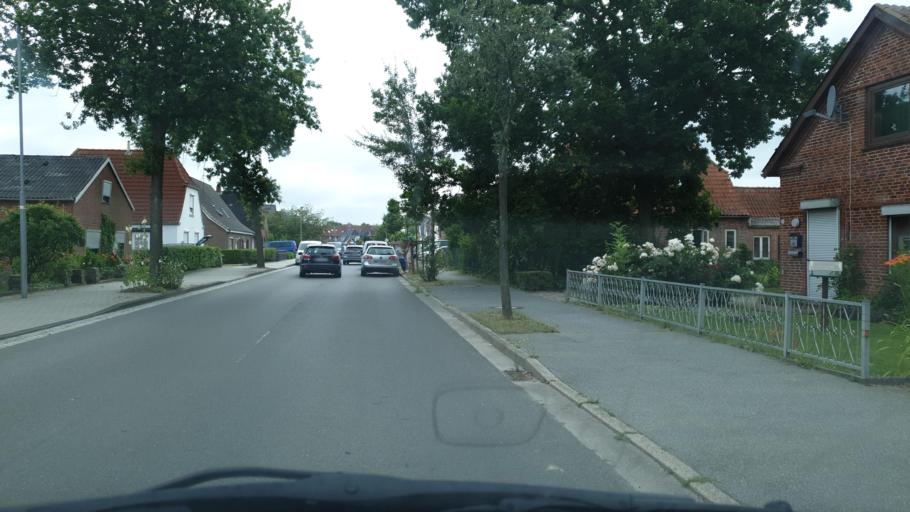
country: DE
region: Schleswig-Holstein
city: Friedrichskoog
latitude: 54.0084
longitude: 8.8844
